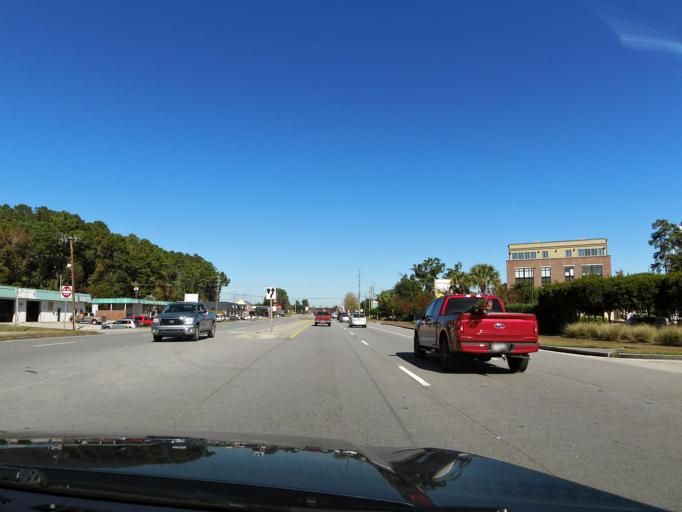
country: US
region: Georgia
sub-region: Bryan County
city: Richmond Hill
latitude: 31.9454
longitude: -81.3150
